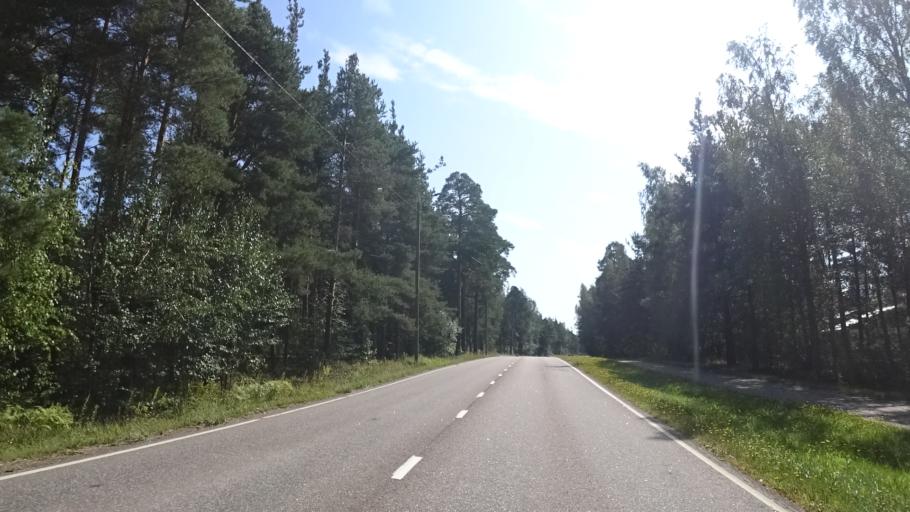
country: FI
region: Kymenlaakso
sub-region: Kotka-Hamina
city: Karhula
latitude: 60.5017
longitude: 26.9642
